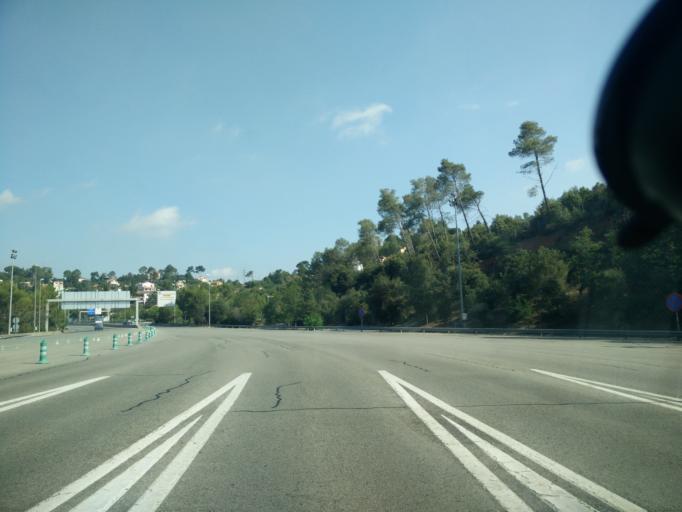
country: ES
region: Catalonia
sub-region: Provincia de Barcelona
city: Sant Cugat del Valles
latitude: 41.4374
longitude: 2.0754
